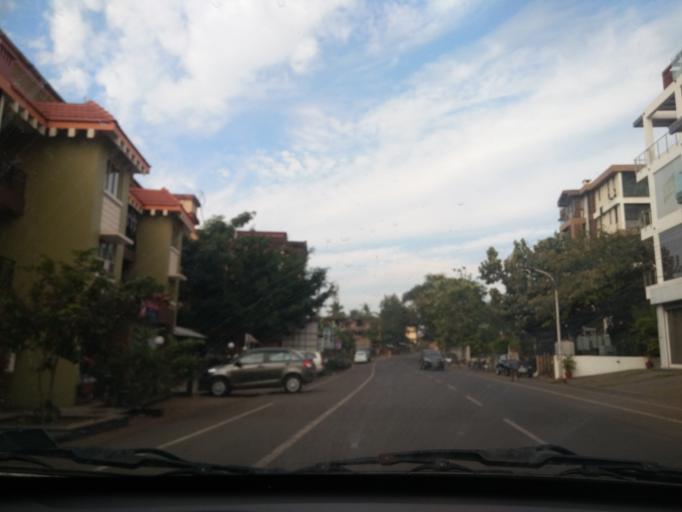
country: IN
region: Goa
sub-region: South Goa
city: Raia
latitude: 15.2899
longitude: 73.9702
